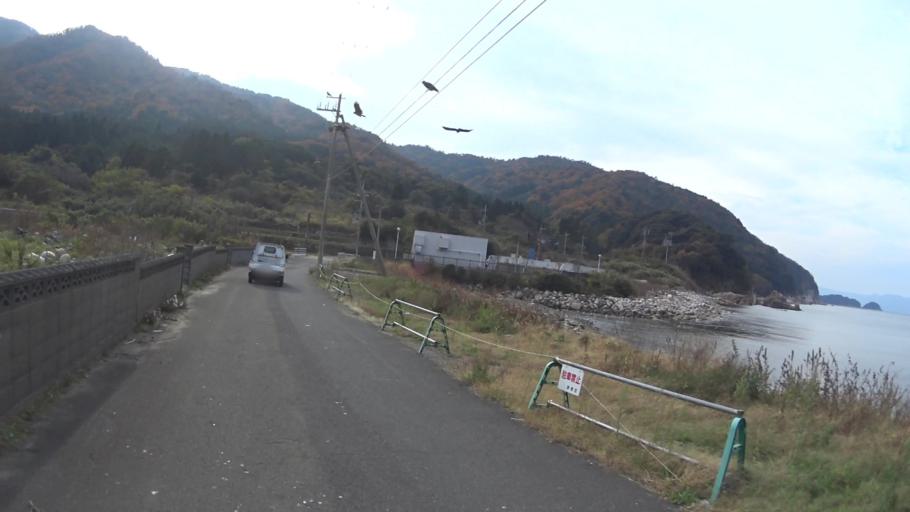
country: JP
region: Kyoto
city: Maizuru
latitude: 35.5668
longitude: 135.4273
